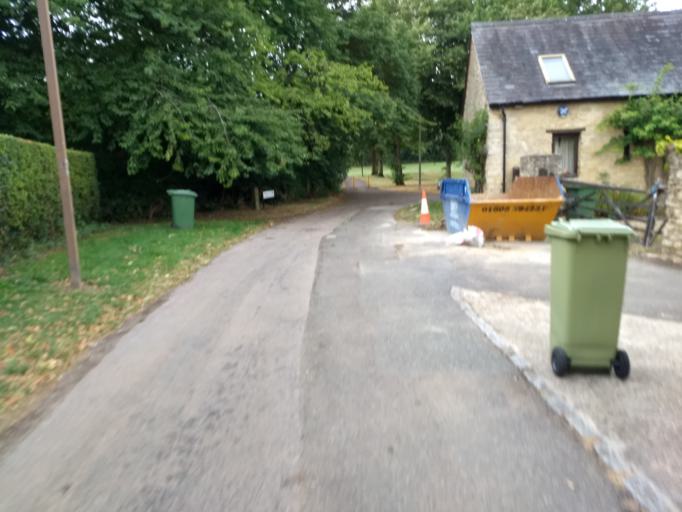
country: GB
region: England
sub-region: Milton Keynes
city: Milton Keynes
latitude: 52.0674
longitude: -0.7531
